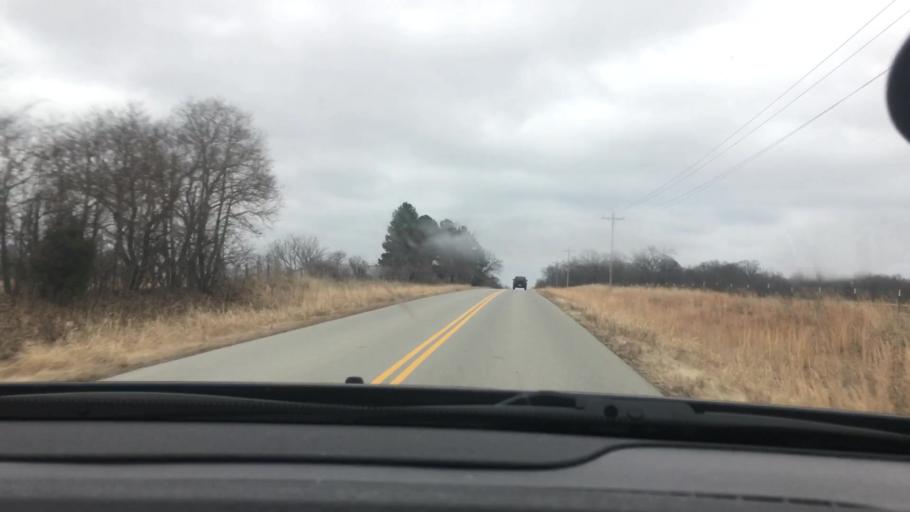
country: US
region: Oklahoma
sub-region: Atoka County
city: Atoka
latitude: 34.3277
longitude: -96.0755
